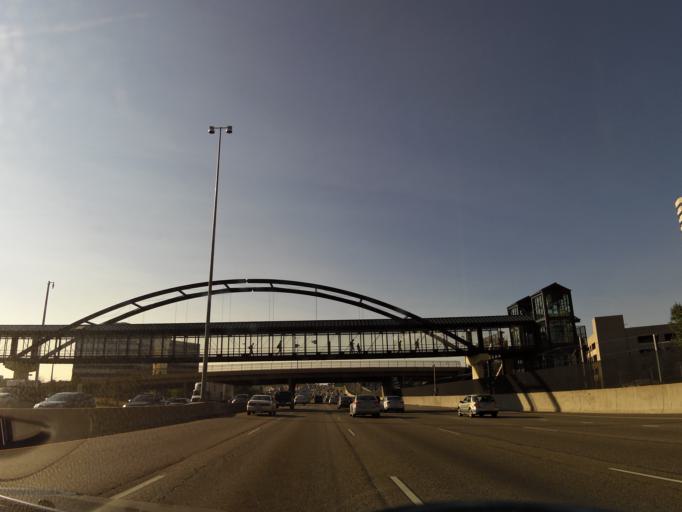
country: US
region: Colorado
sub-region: Arapahoe County
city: Castlewood
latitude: 39.6017
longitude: -104.8889
